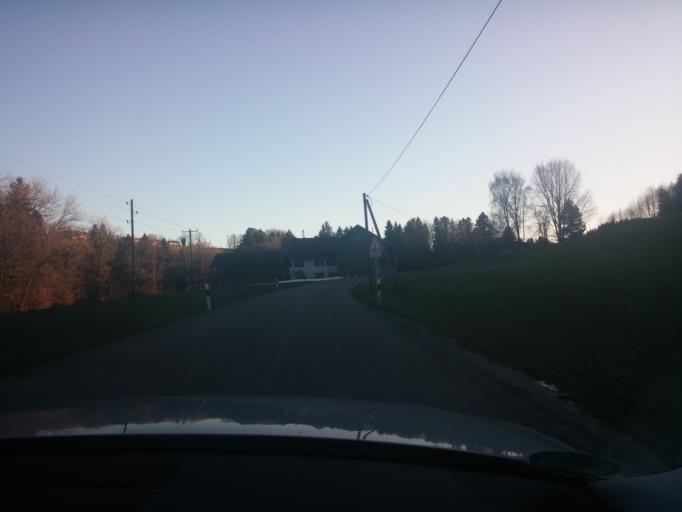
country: DE
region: Bavaria
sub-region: Swabia
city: Altusried
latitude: 47.8248
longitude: 10.1773
